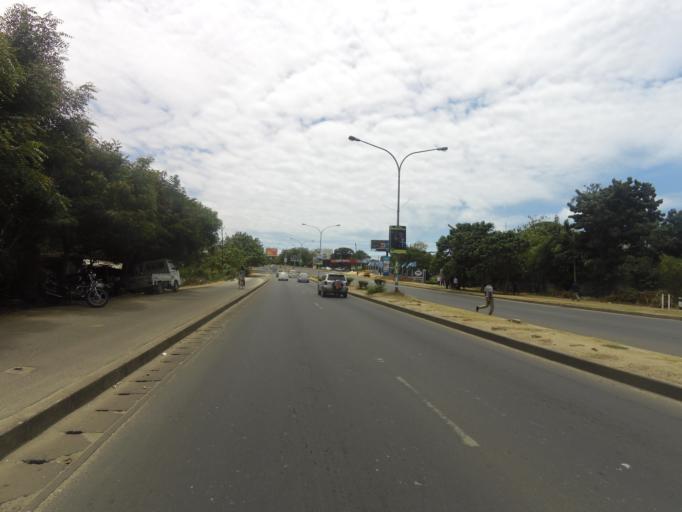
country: TZ
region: Dar es Salaam
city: Magomeni
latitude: -6.7840
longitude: 39.2764
